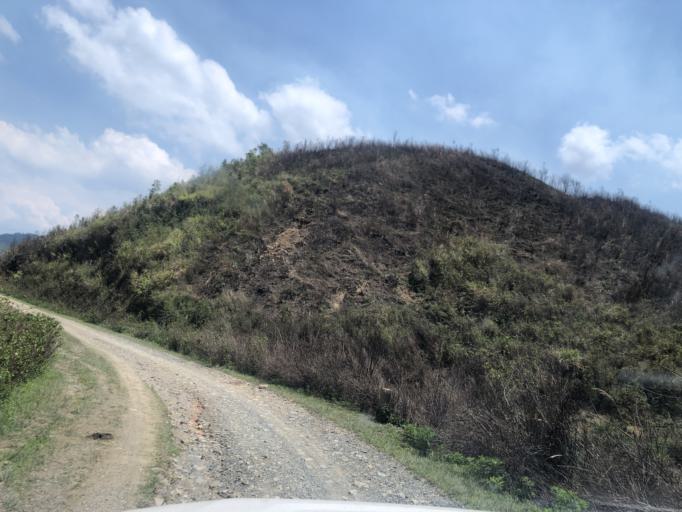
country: LA
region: Phongsali
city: Phongsali
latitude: 21.4109
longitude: 102.1863
